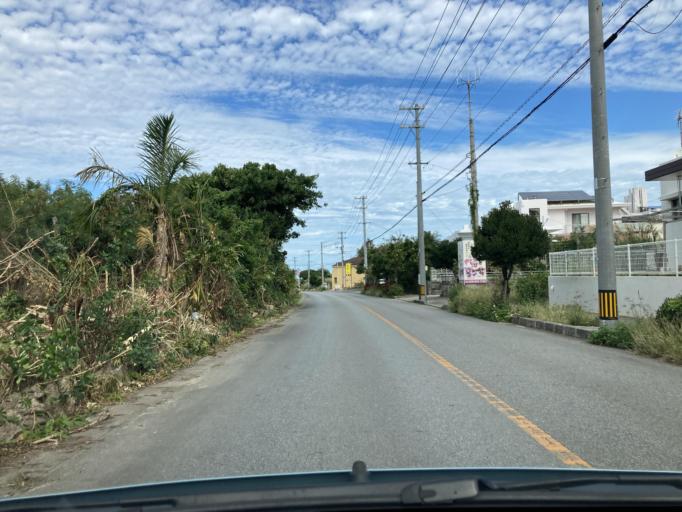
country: JP
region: Okinawa
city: Ishikawa
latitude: 26.4287
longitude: 127.7293
